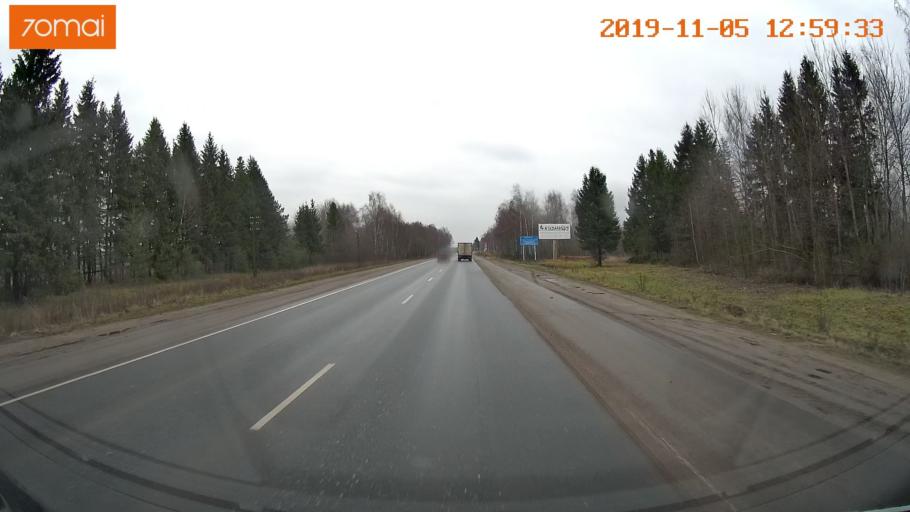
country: RU
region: Ivanovo
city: Kokhma
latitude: 56.9178
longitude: 41.1313
